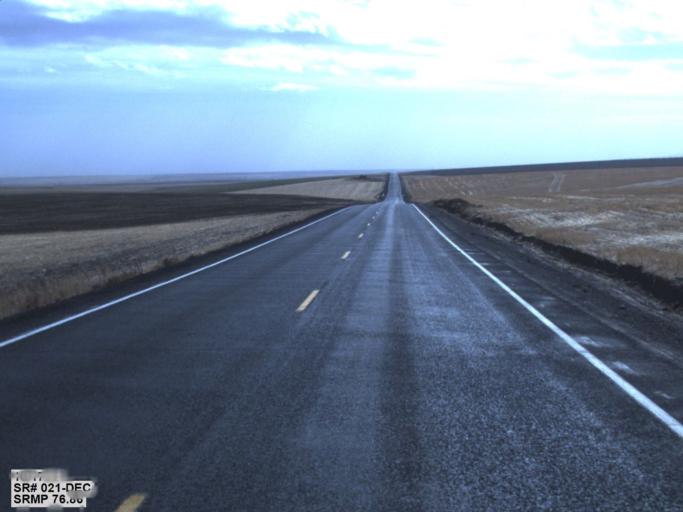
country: US
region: Washington
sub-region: Okanogan County
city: Coulee Dam
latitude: 47.5942
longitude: -118.7861
